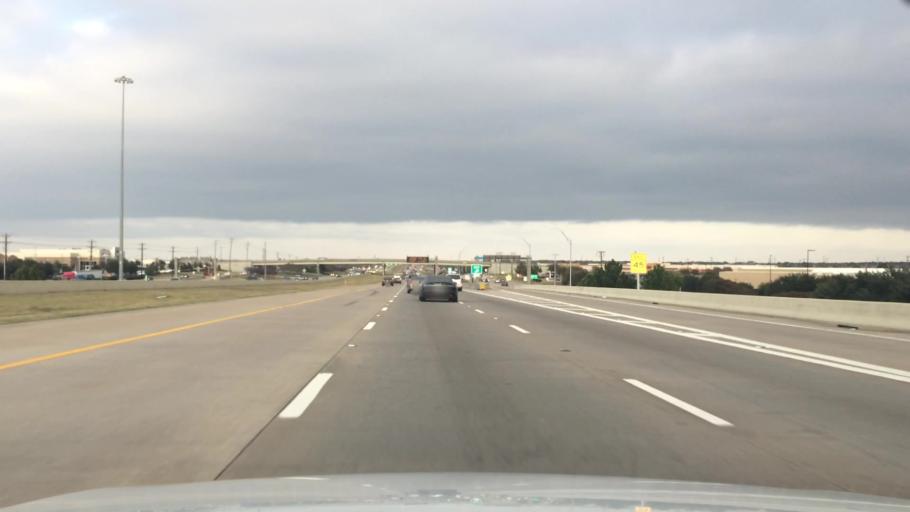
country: US
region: Texas
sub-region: Collin County
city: Frisco
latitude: 33.0980
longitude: -96.8028
